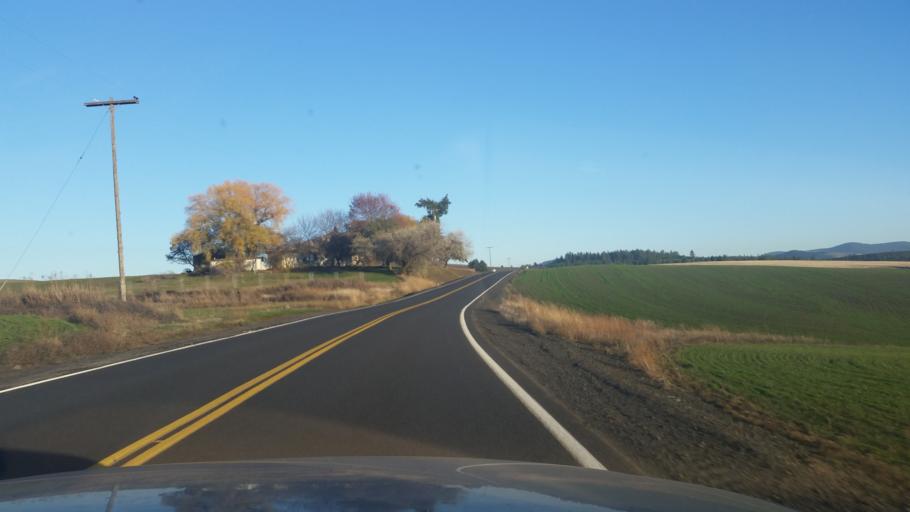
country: US
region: Washington
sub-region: Spokane County
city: Opportunity
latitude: 47.3510
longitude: -117.2380
